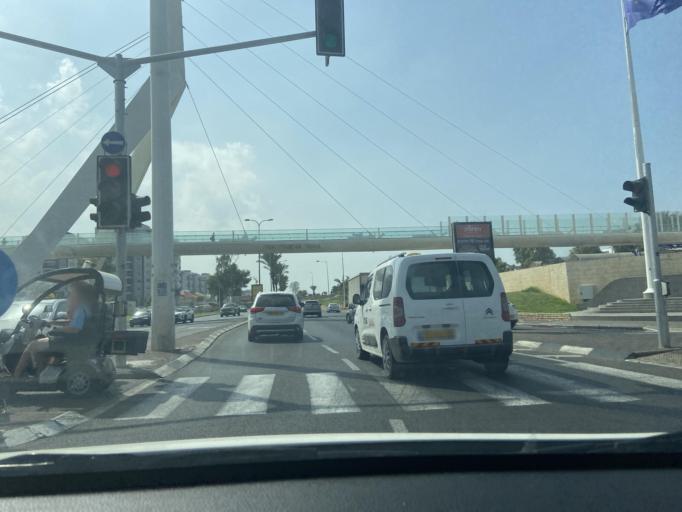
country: IL
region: Northern District
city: Nahariya
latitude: 33.0058
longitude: 35.0994
